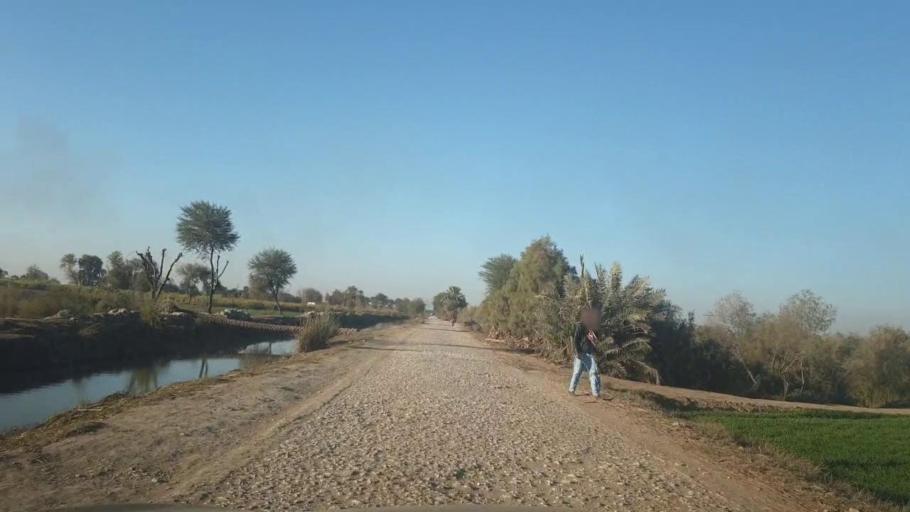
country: PK
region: Sindh
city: Ghotki
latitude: 28.0004
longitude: 69.2709
